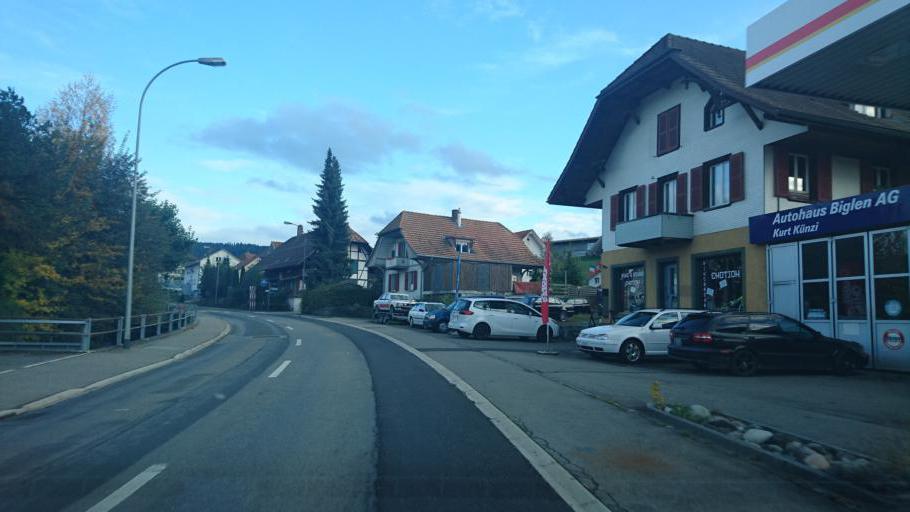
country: CH
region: Bern
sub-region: Bern-Mittelland District
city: Biglen
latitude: 46.9275
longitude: 7.6215
